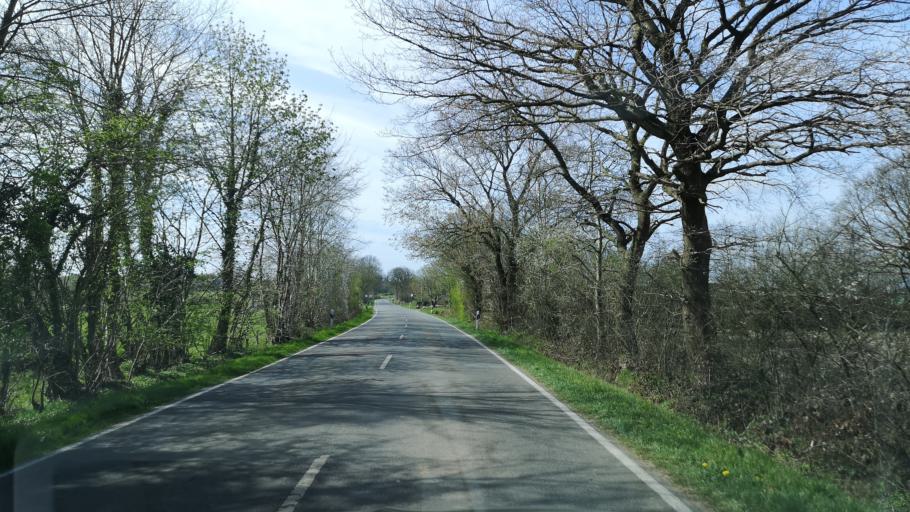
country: DE
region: Schleswig-Holstein
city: Osterrade
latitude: 54.1921
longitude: 9.3623
